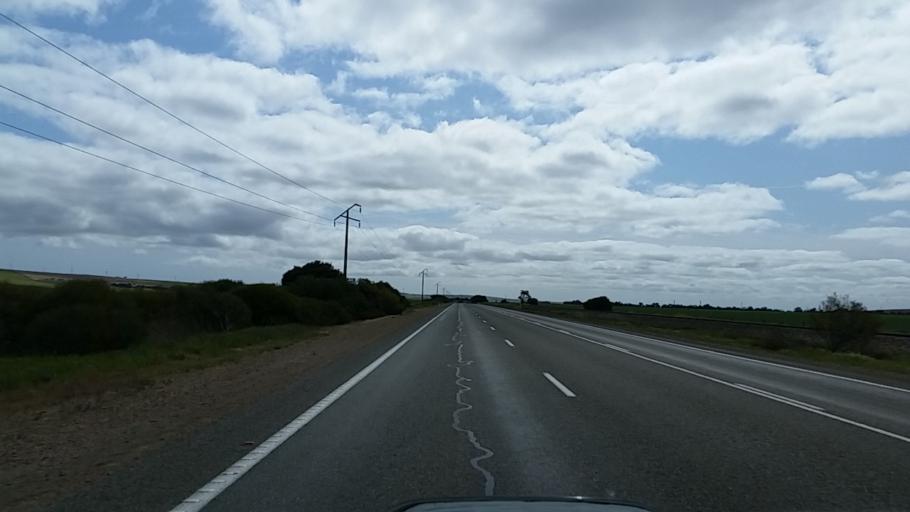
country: AU
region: South Australia
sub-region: Port Pirie City and Dists
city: Crystal Brook
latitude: -33.5299
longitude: 138.2067
